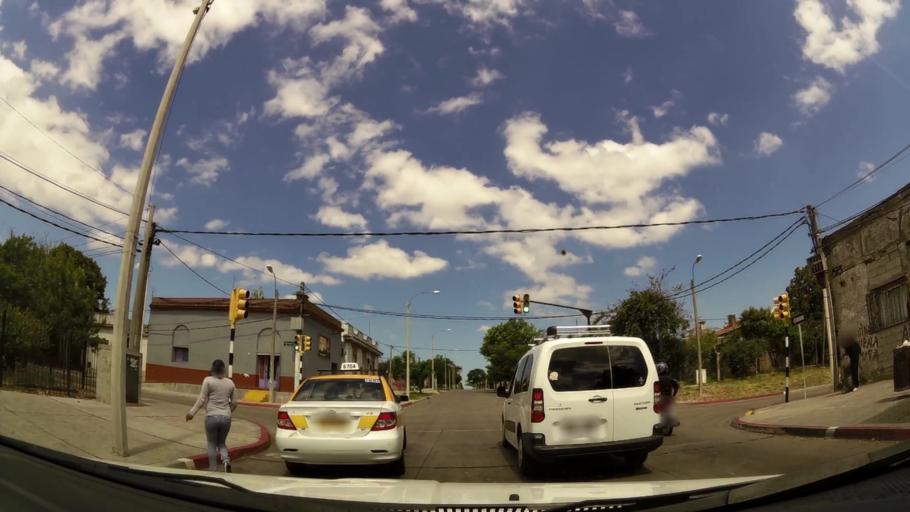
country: UY
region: Montevideo
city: Montevideo
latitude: -34.8428
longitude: -56.2435
